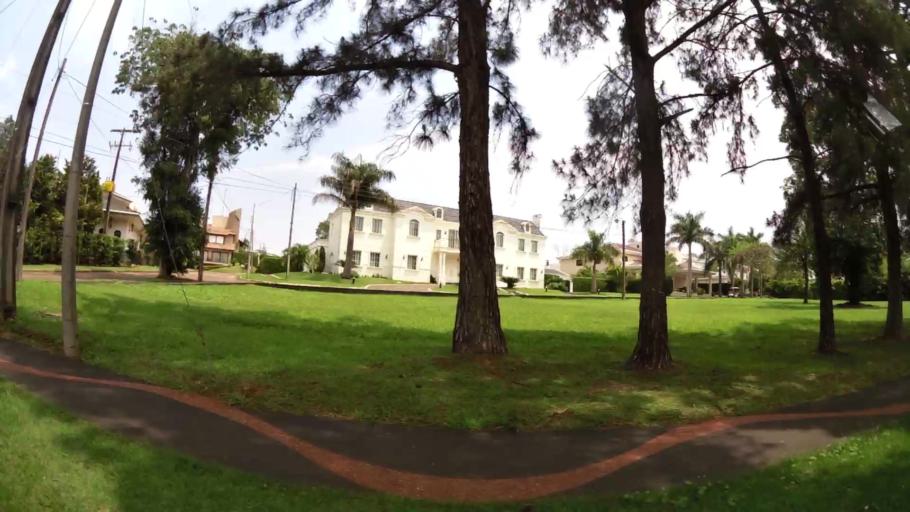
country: PY
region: Alto Parana
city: Ciudad del Este
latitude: -25.4845
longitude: -54.6178
